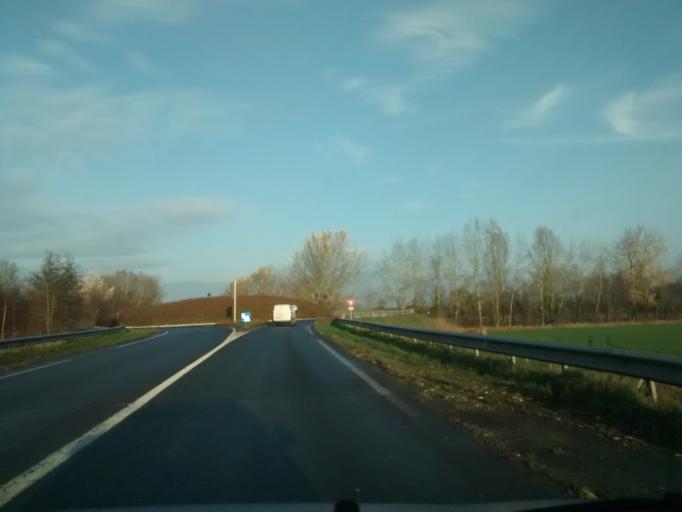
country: FR
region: Lower Normandy
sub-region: Departement de la Manche
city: Pontorson
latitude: 48.5599
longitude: -1.5299
